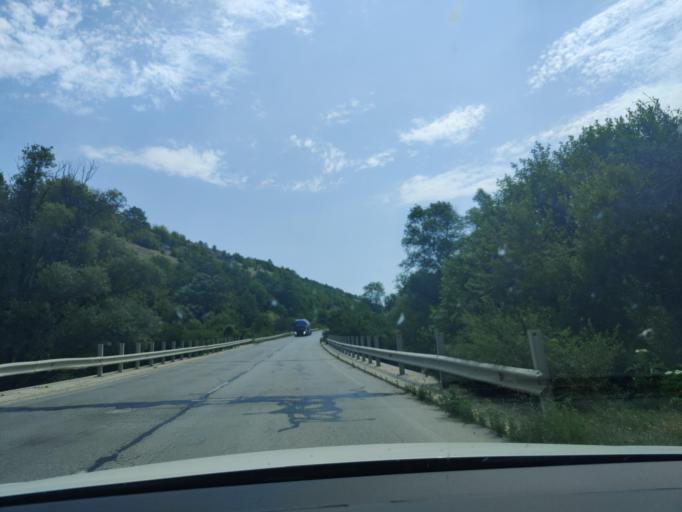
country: BG
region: Vidin
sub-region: Obshtina Ruzhintsi
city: Ruzhintsi
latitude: 43.5667
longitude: 22.9180
